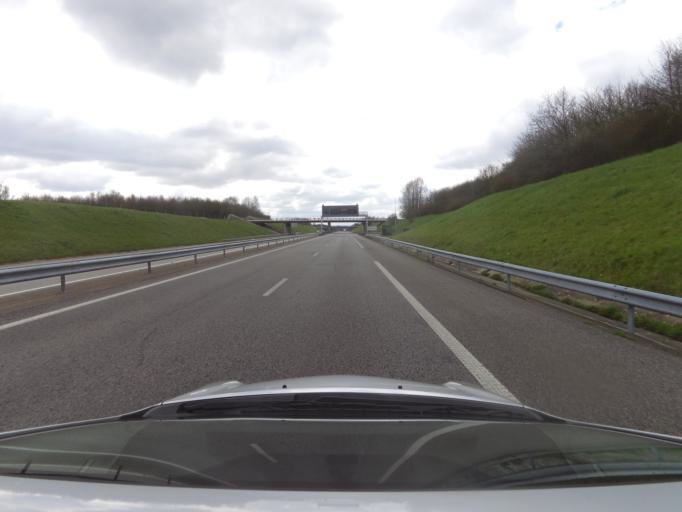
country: FR
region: Haute-Normandie
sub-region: Departement de la Seine-Maritime
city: Saint-Aubin-Routot
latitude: 49.5219
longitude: 0.3042
